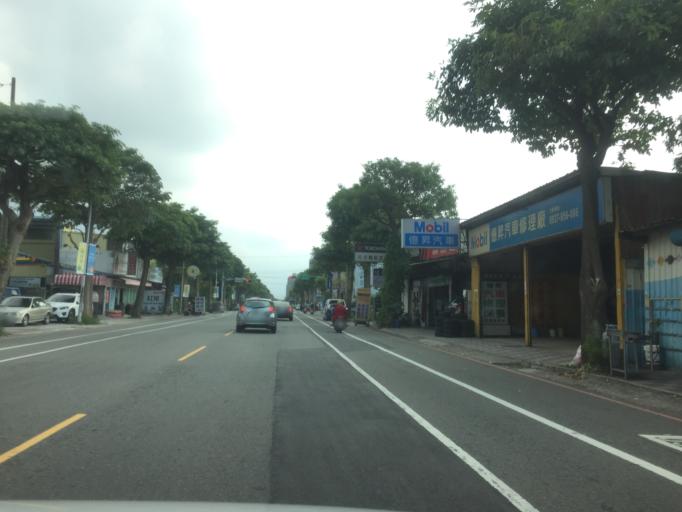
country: TW
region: Taiwan
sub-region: Taoyuan
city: Taoyuan
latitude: 24.9707
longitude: 121.3068
